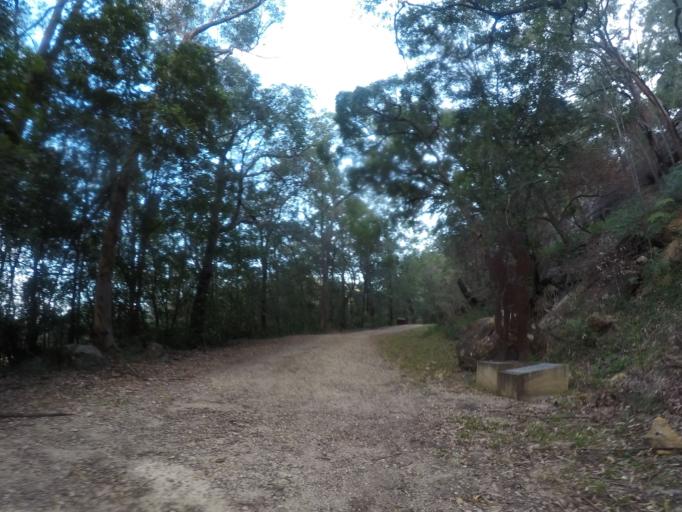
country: AU
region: New South Wales
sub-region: Hornsby Shire
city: Glenorie
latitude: -33.3743
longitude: 150.9846
